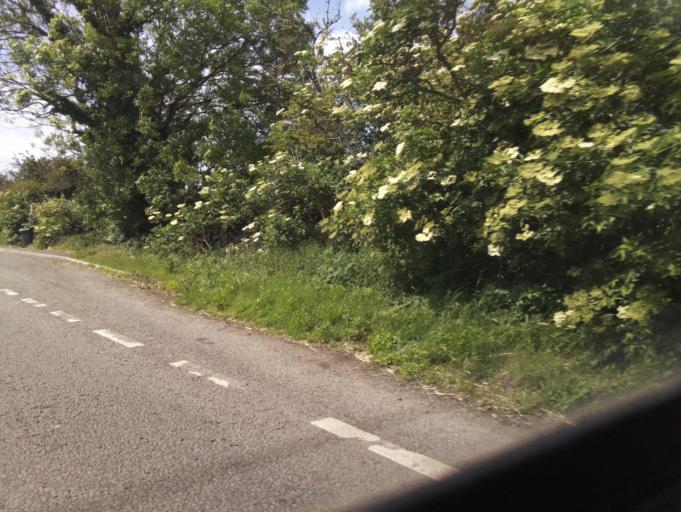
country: GB
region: England
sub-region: Lincolnshire
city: Burton
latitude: 53.3412
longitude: -0.5442
